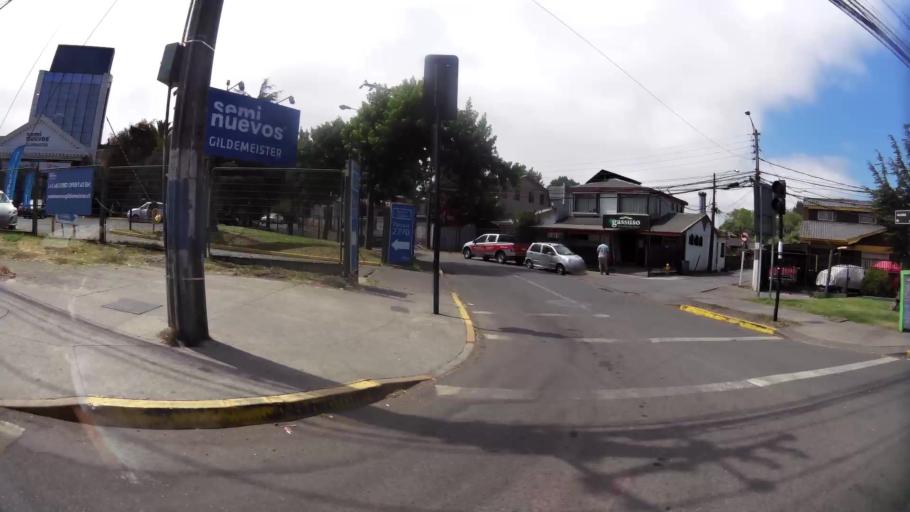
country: CL
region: Biobio
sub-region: Provincia de Concepcion
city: Concepcion
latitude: -36.8012
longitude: -73.0564
